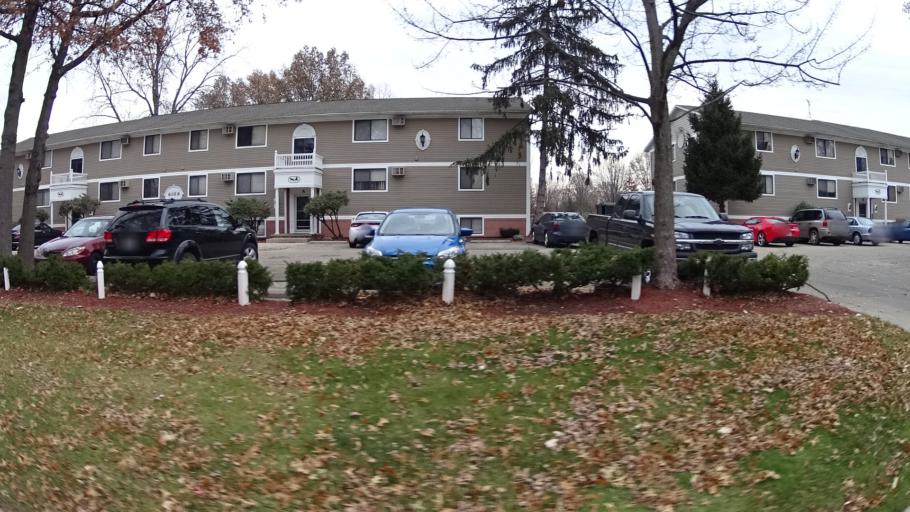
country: US
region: Ohio
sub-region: Lorain County
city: North Ridgeville
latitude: 41.4008
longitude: -82.0086
